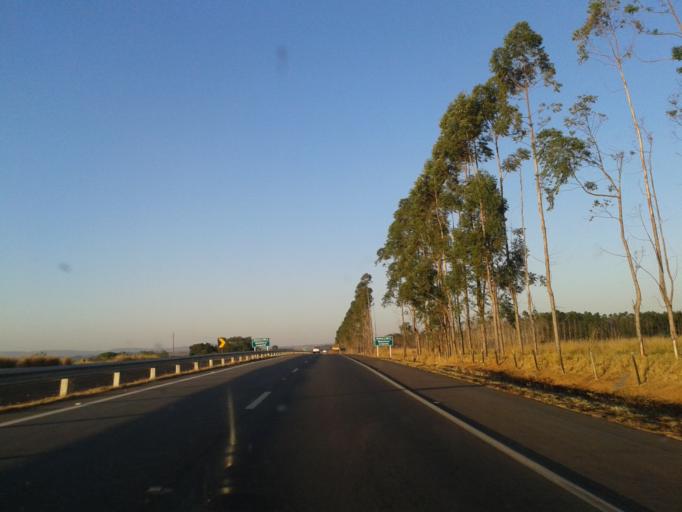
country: BR
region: Goias
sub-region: Itaberai
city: Itaberai
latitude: -16.0103
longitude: -49.9683
